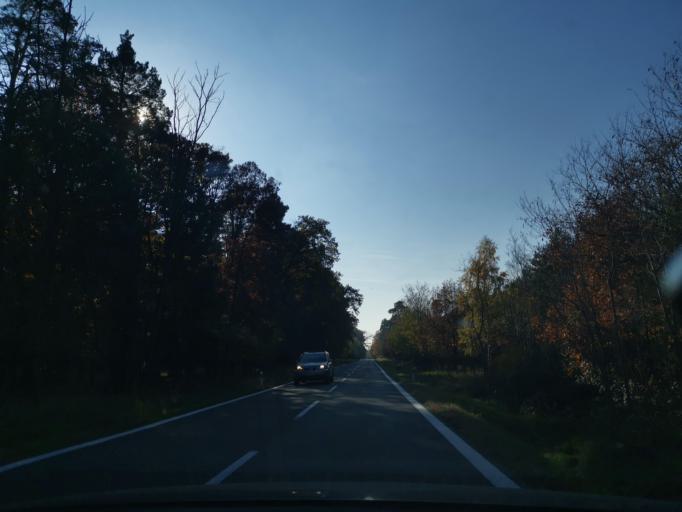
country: SK
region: Bratislavsky
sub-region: Okres Malacky
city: Malacky
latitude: 48.4720
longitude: 17.0519
